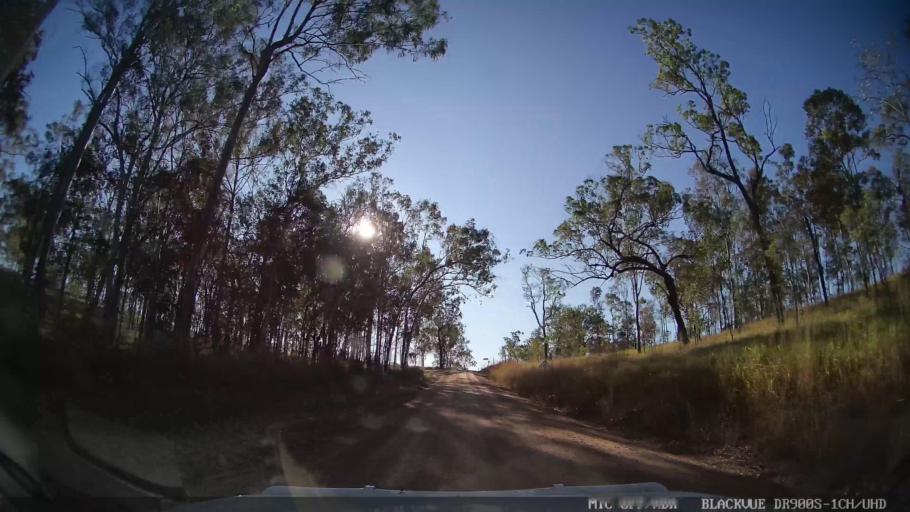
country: AU
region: Queensland
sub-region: Bundaberg
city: Sharon
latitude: -24.7906
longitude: 151.6088
